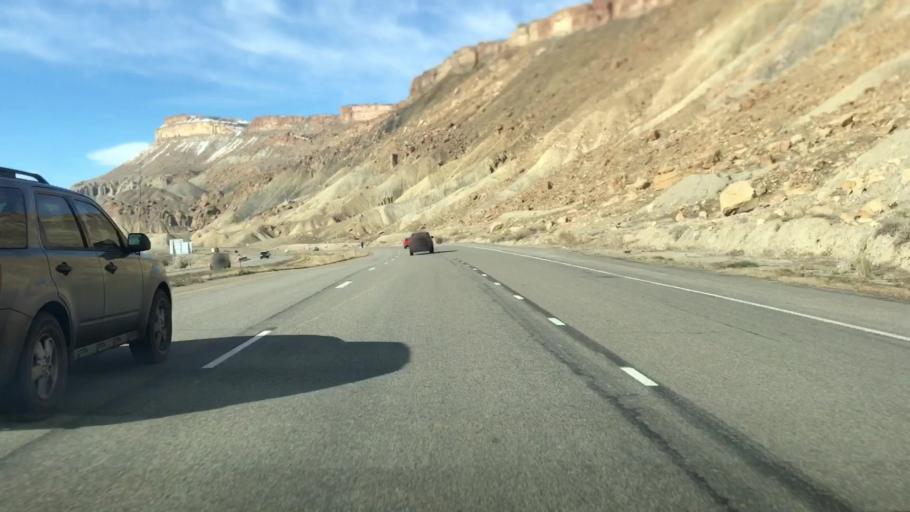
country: US
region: Colorado
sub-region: Mesa County
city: Palisade
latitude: 39.1194
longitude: -108.3639
